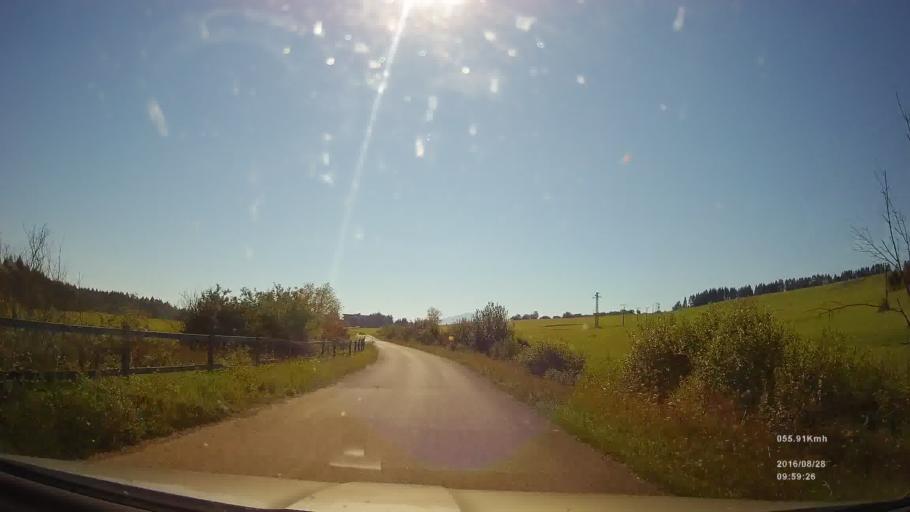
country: SK
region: Zilinsky
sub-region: Okres Liptovsky Mikulas
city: Liptovsky Mikulas
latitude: 49.1130
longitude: 19.4844
